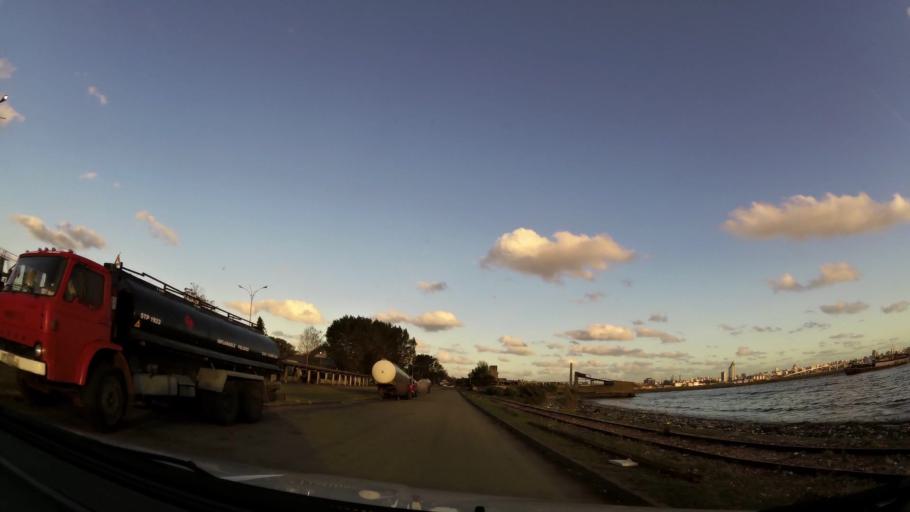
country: UY
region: Montevideo
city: Montevideo
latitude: -34.8728
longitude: -56.2229
